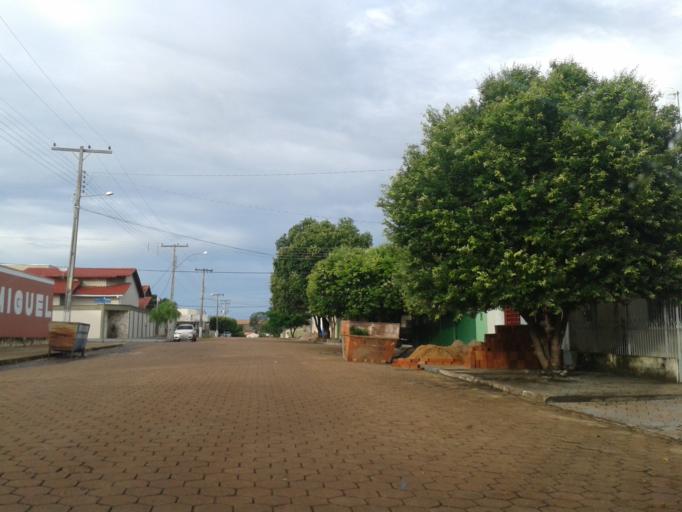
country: BR
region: Goias
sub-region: Sao Miguel Do Araguaia
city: Sao Miguel do Araguaia
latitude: -13.2716
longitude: -50.1634
